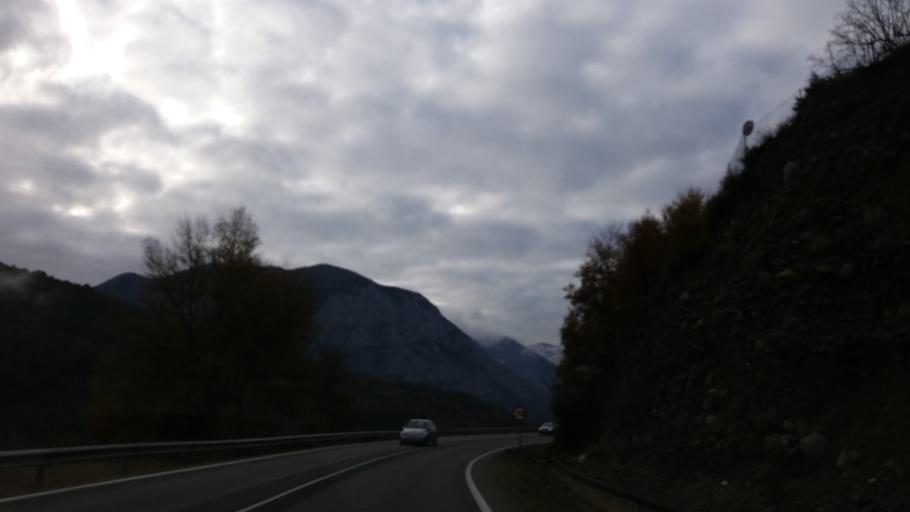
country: ES
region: Catalonia
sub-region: Provincia de Lleida
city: Coll de Nargo
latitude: 42.2153
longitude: 1.3329
